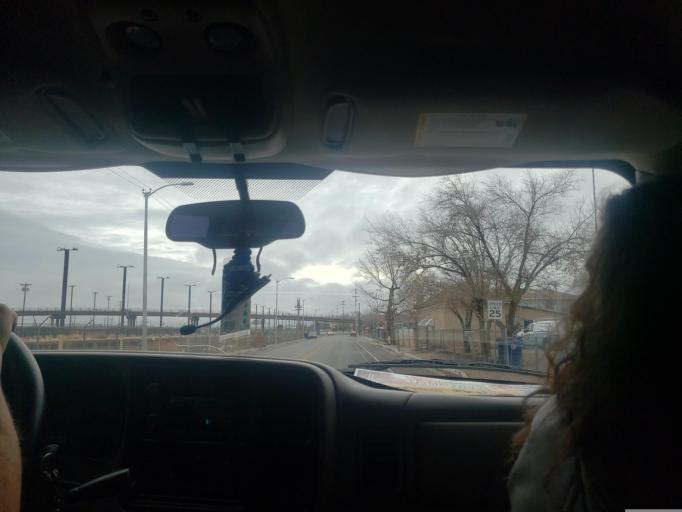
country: US
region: New Mexico
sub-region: Bernalillo County
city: Albuquerque
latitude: 35.0721
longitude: -106.6519
